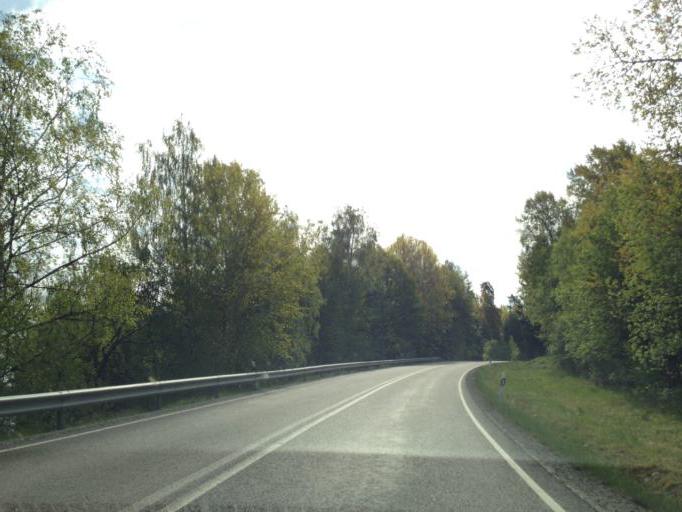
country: SE
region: Soedermanland
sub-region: Nykopings Kommun
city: Stigtomta
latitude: 58.9718
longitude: 16.8494
